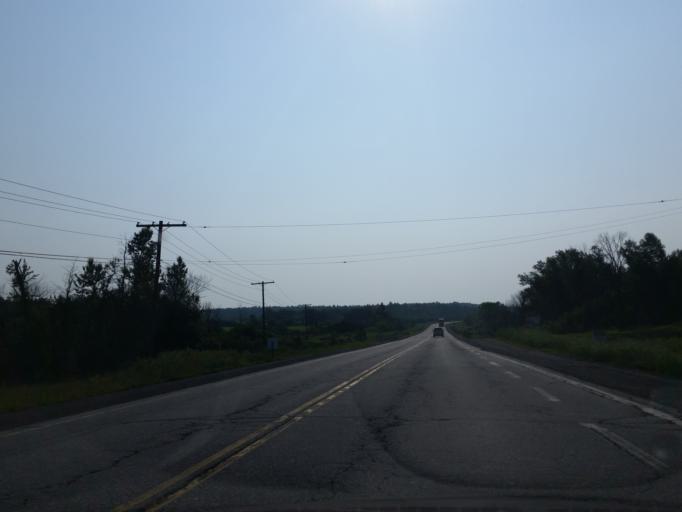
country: CA
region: Ontario
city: Greater Sudbury
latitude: 46.4304
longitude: -80.2316
